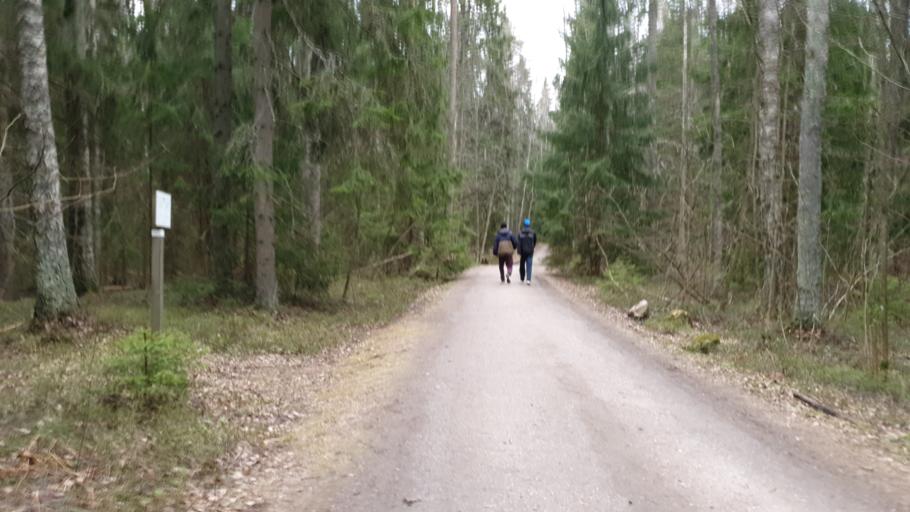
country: FI
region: Uusimaa
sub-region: Helsinki
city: Helsinki
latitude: 60.2698
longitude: 24.9257
